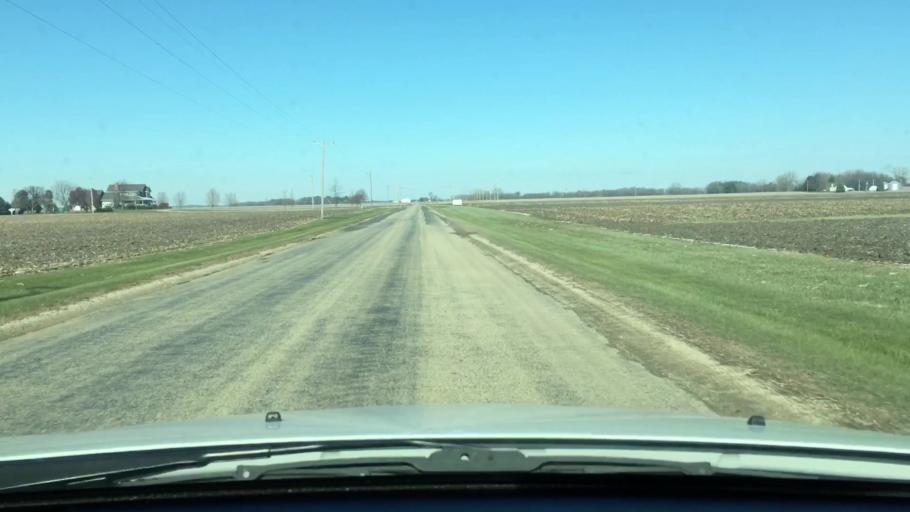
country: US
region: Illinois
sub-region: Ogle County
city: Hillcrest
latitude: 41.9728
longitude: -89.0009
